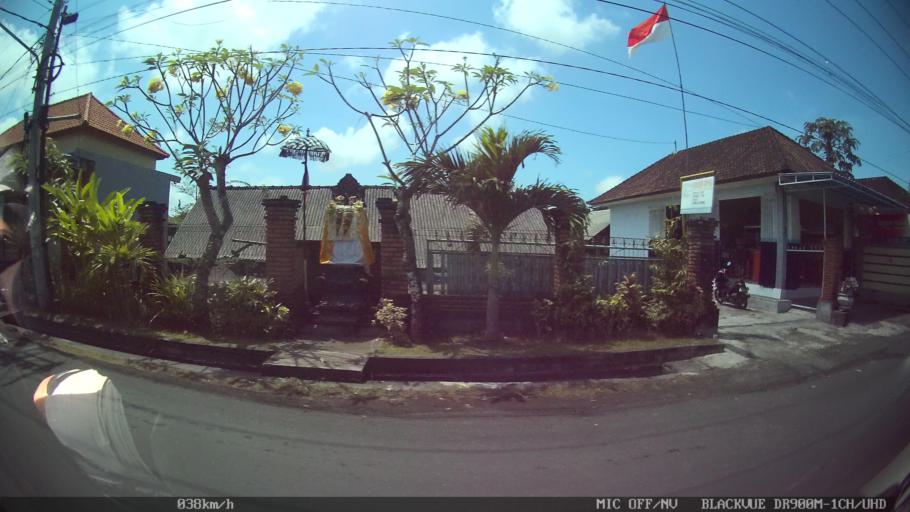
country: ID
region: Bali
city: Banjar Jabejero
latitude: -8.6068
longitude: 115.2588
